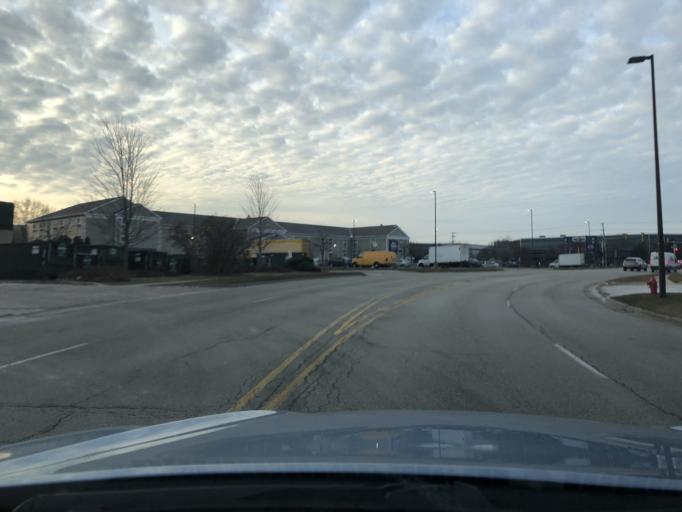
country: US
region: Illinois
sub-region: Cook County
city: Elk Grove Village
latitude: 42.0116
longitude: -87.9430
